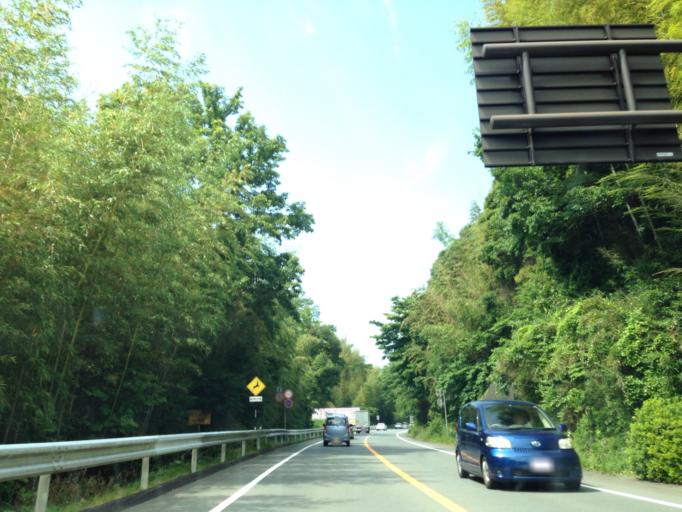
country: JP
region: Shizuoka
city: Mishima
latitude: 35.0463
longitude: 138.9210
